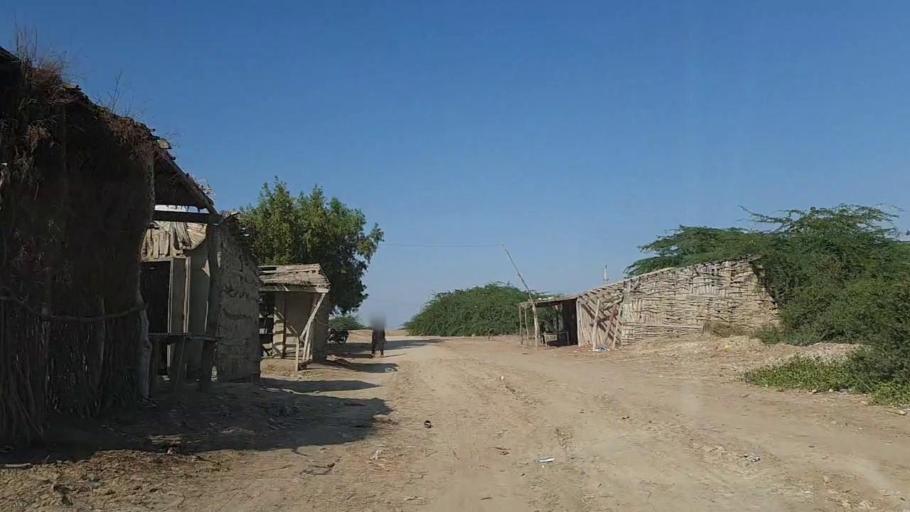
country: PK
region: Sindh
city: Chuhar Jamali
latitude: 24.5482
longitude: 68.0156
